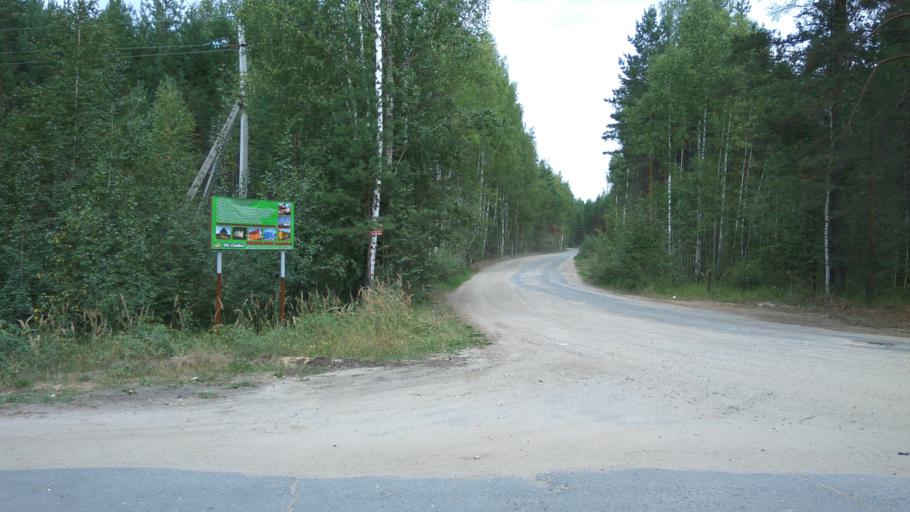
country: RU
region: Mariy-El
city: Surok
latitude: 56.4295
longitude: 48.0889
